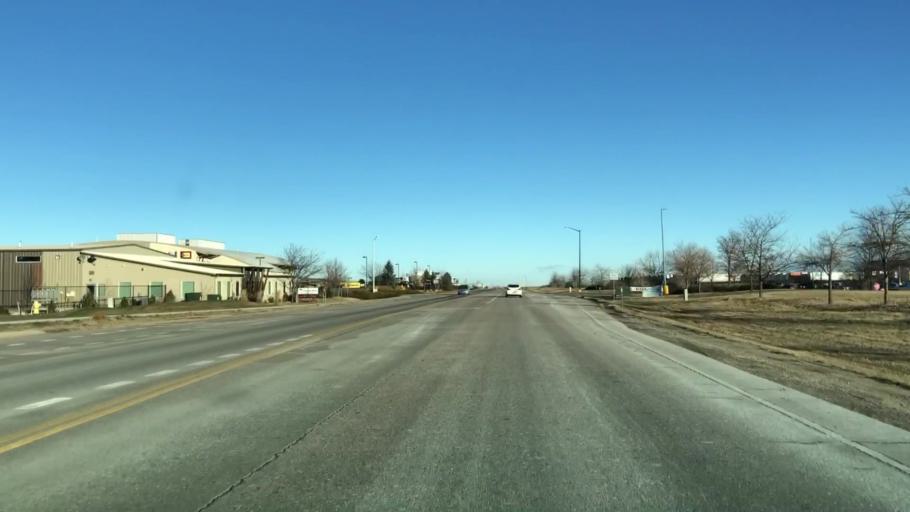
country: US
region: Colorado
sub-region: Weld County
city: Windsor
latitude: 40.4359
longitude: -104.9719
